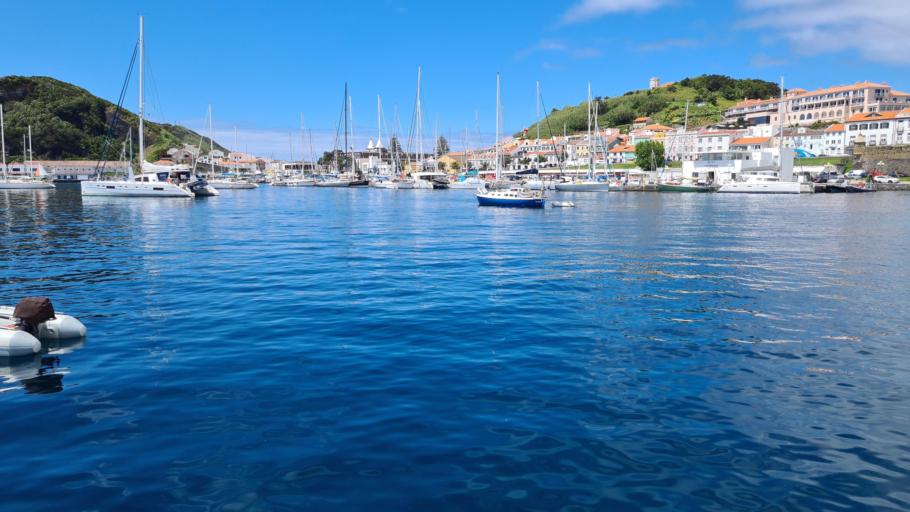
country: PT
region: Azores
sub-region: Horta
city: Horta
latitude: 38.5317
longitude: -28.6240
